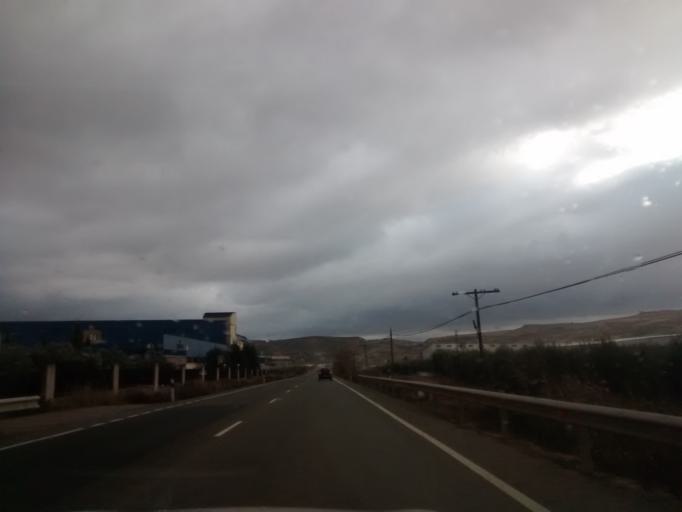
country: ES
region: La Rioja
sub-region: Provincia de La Rioja
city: Fuenmayor
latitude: 42.4646
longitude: -2.6010
